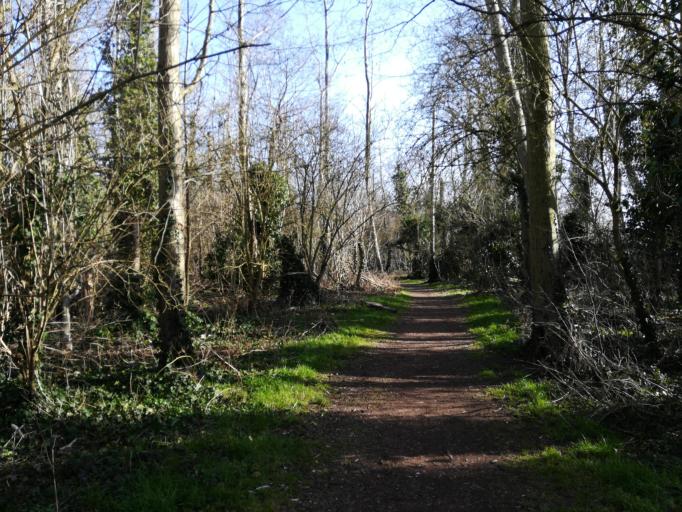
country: FR
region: Nord-Pas-de-Calais
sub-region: Departement du Pas-de-Calais
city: Henin-Beaumont
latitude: 50.4062
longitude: 2.9532
